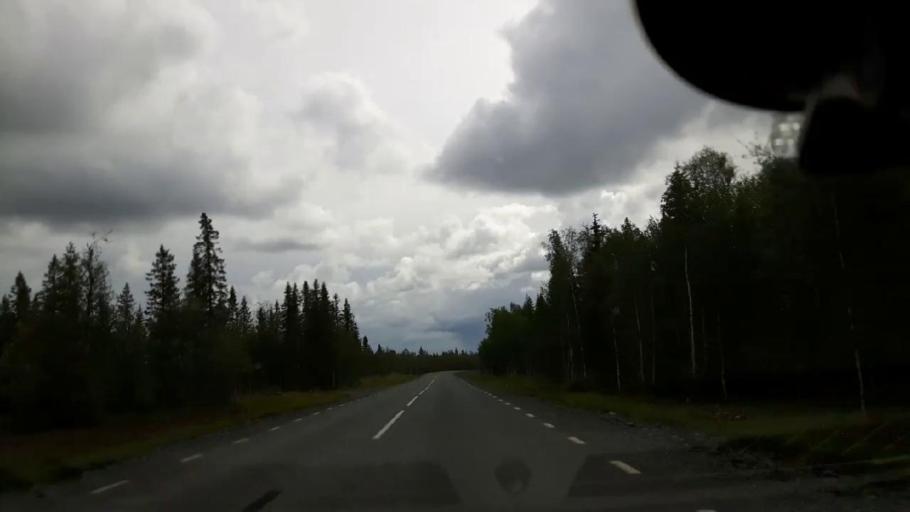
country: SE
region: Jaemtland
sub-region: Krokoms Kommun
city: Valla
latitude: 63.4576
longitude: 13.8283
